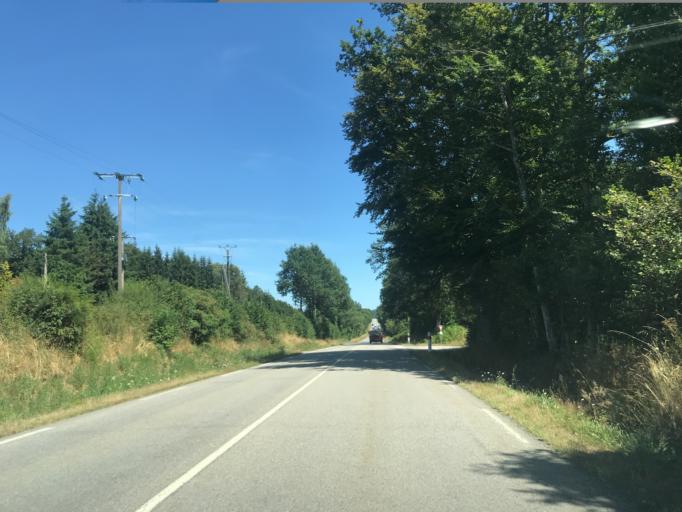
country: FR
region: Limousin
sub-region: Departement de la Correze
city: Meymac
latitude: 45.4888
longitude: 2.2013
